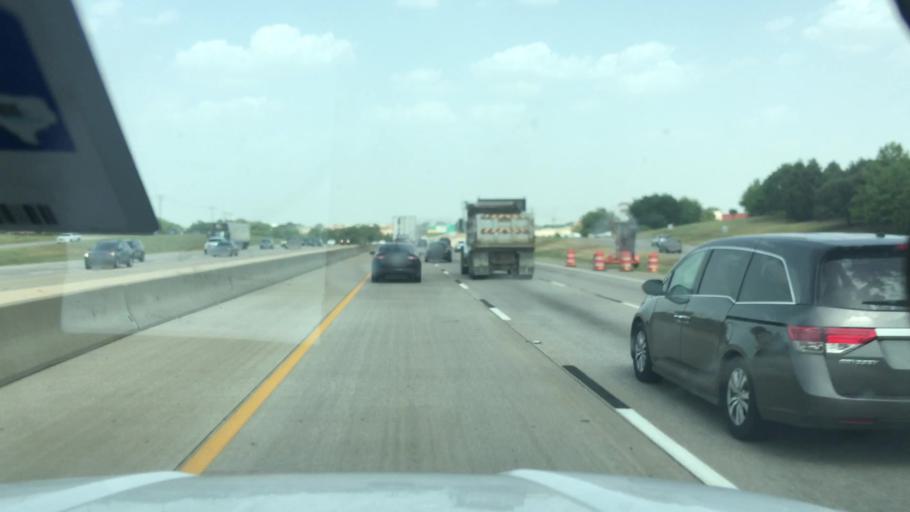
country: US
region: Texas
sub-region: Tarrant County
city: Southlake
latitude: 32.9432
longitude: -97.1121
